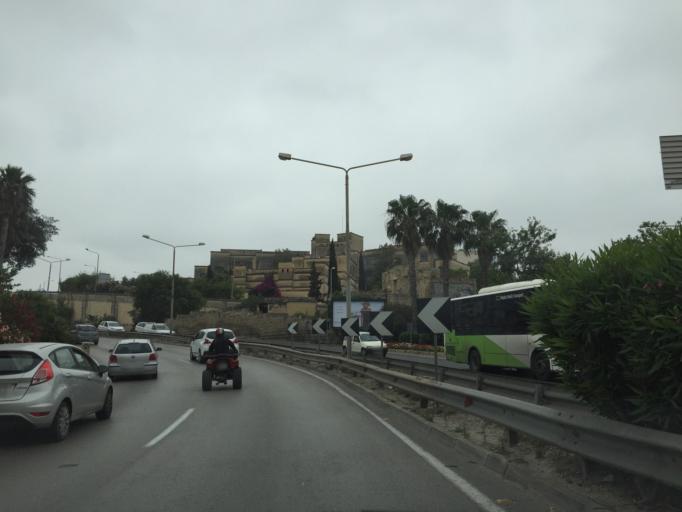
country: MT
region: L-Imsida
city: Imsida
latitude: 35.8946
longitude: 14.4822
